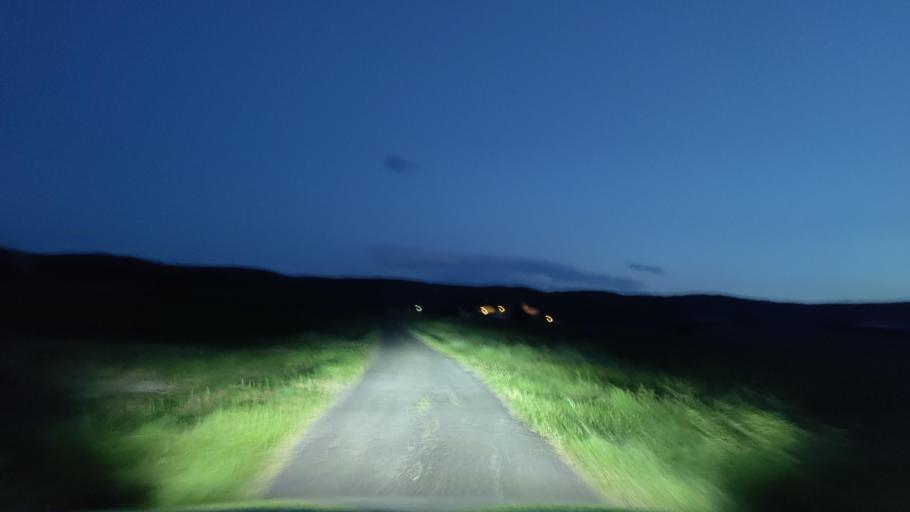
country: FR
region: Languedoc-Roussillon
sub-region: Departement des Pyrenees-Orientales
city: Estagel
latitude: 42.8659
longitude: 2.7255
